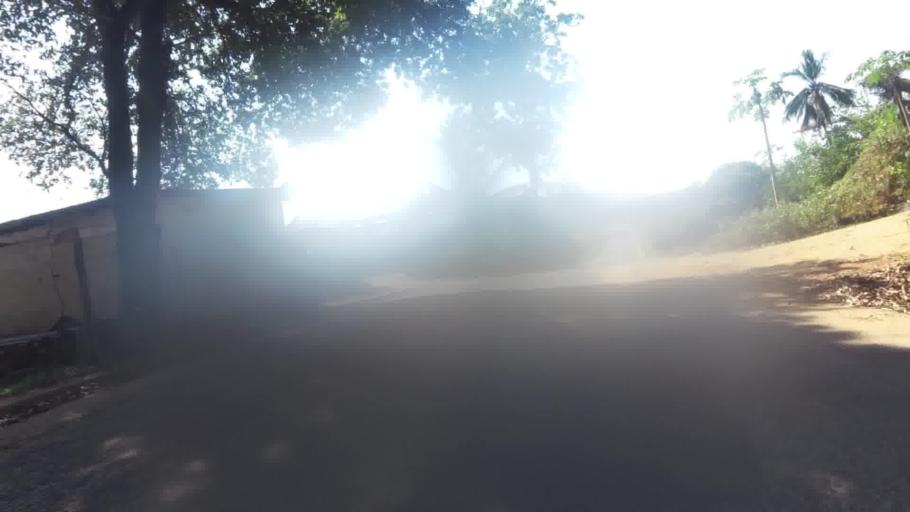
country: BR
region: Espirito Santo
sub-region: Alfredo Chaves
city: Alfredo Chaves
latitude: -20.6549
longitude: -40.7589
